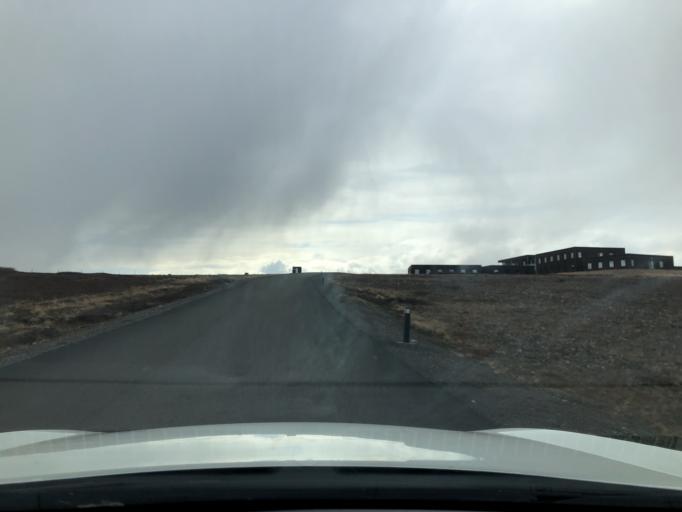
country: IS
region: Northeast
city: Laugar
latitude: 65.5736
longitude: -17.0868
